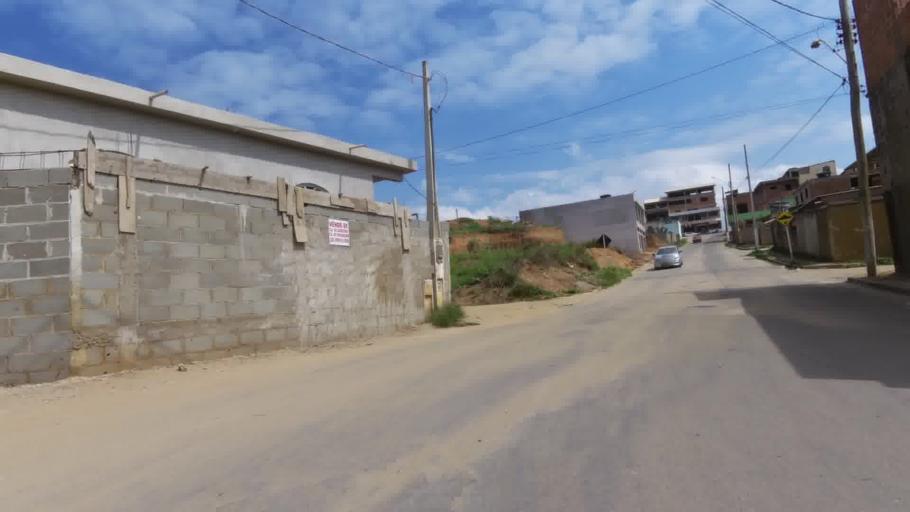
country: BR
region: Espirito Santo
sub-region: Itapemirim
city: Itapemirim
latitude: -21.0240
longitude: -40.8199
